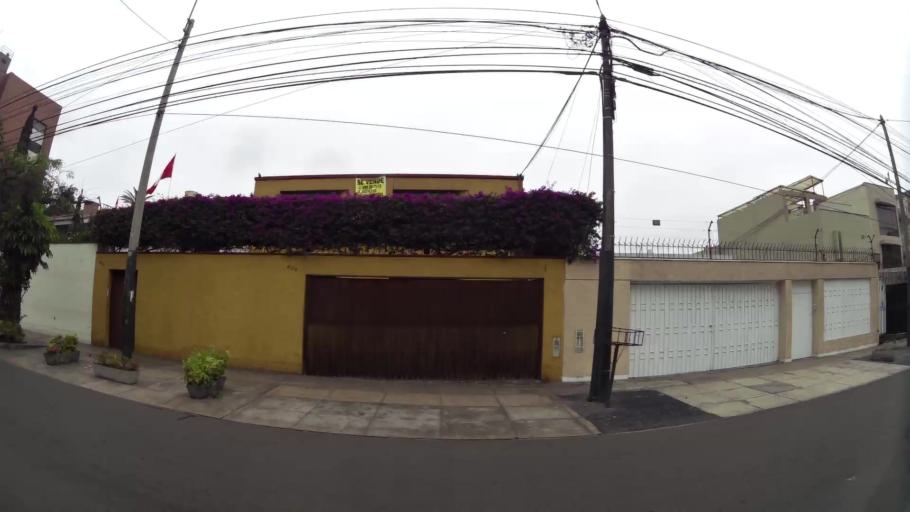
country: PE
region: Lima
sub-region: Lima
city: San Luis
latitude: -12.0997
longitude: -77.0141
